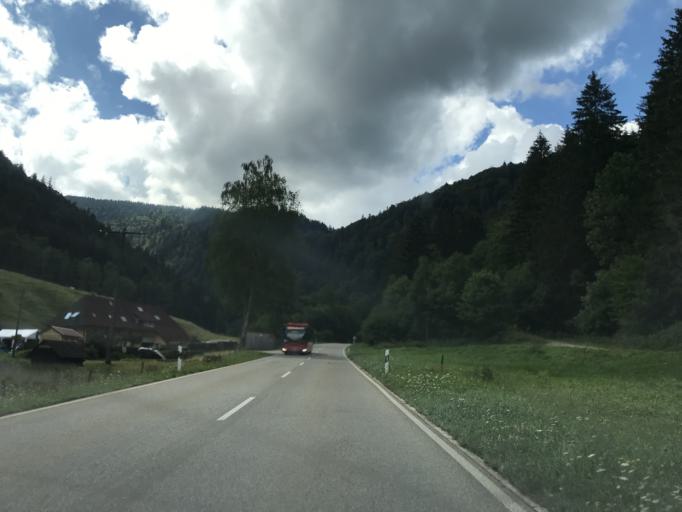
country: DE
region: Baden-Wuerttemberg
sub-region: Freiburg Region
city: Oberried
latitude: 47.9116
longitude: 7.9331
